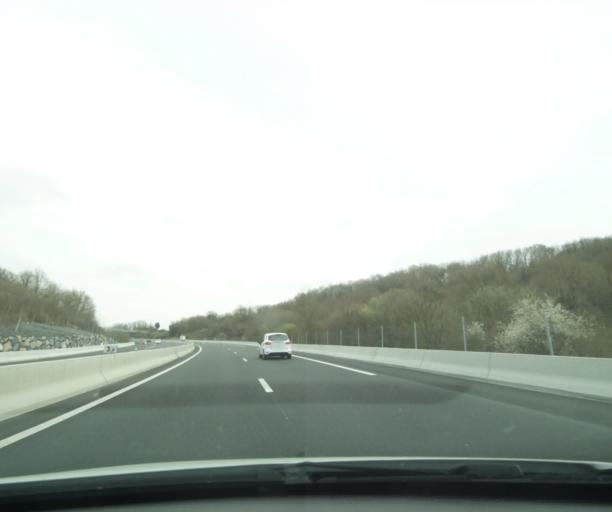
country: FR
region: Aquitaine
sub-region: Departement des Pyrenees-Atlantiques
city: Mouguerre
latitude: 43.4584
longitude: -1.4195
